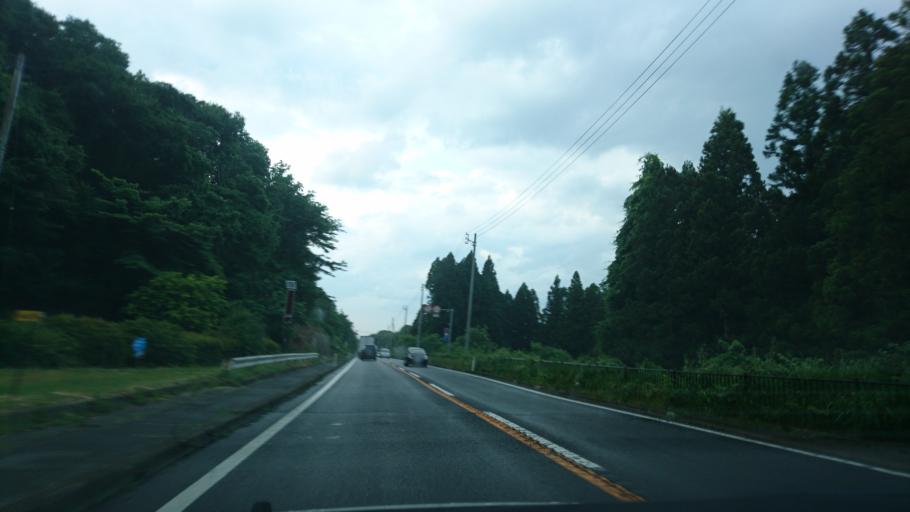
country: JP
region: Iwate
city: Ichinoseki
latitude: 38.9529
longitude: 141.1215
